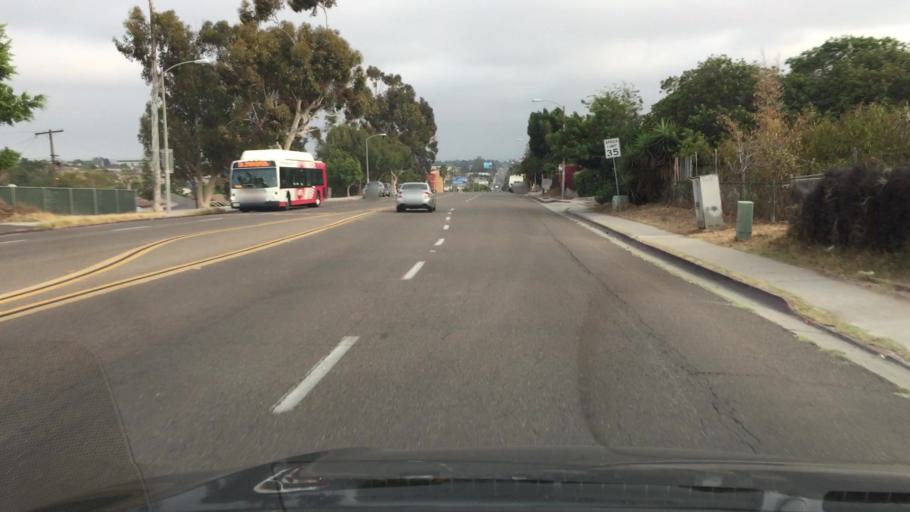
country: US
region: California
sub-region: San Diego County
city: National City
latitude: 32.7148
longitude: -117.0937
